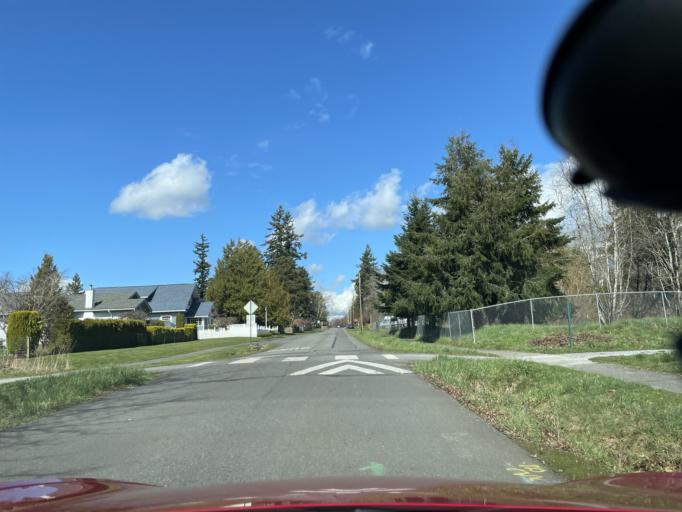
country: US
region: Washington
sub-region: Whatcom County
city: Bellingham
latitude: 48.7654
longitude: -122.4562
